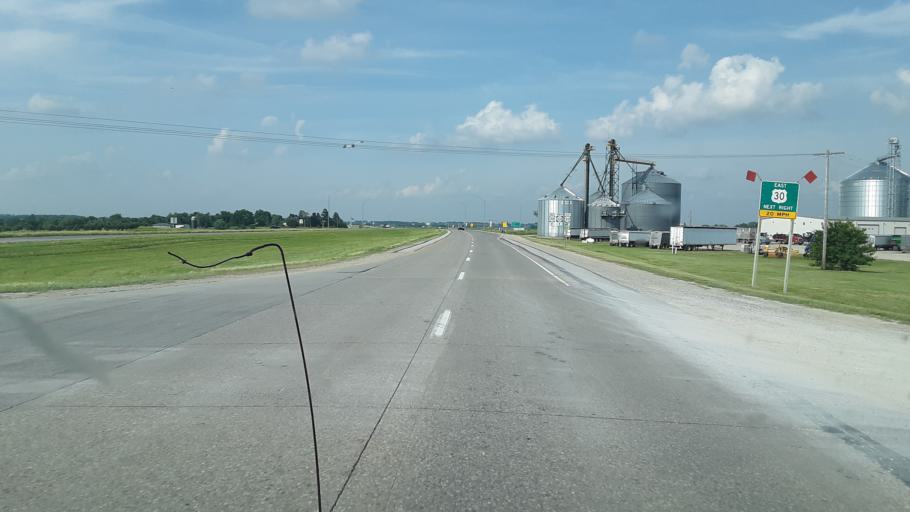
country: US
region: Iowa
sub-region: Marshall County
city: Marshalltown
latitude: 42.0044
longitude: -93.0247
